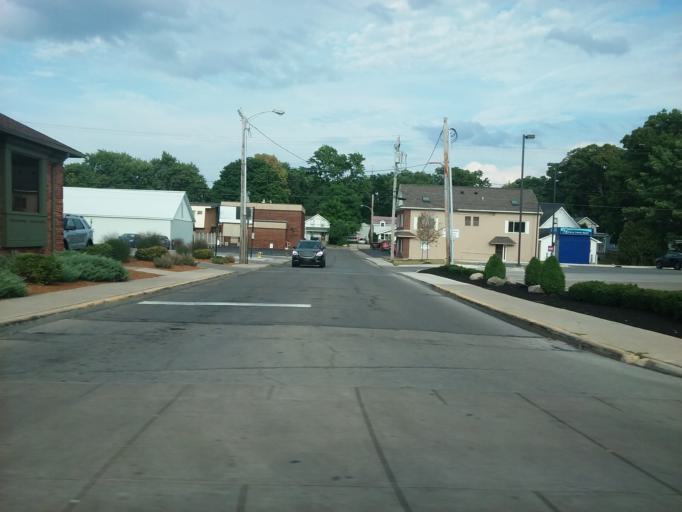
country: US
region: Ohio
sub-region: Wood County
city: Bowling Green
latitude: 41.3720
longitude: -83.6503
